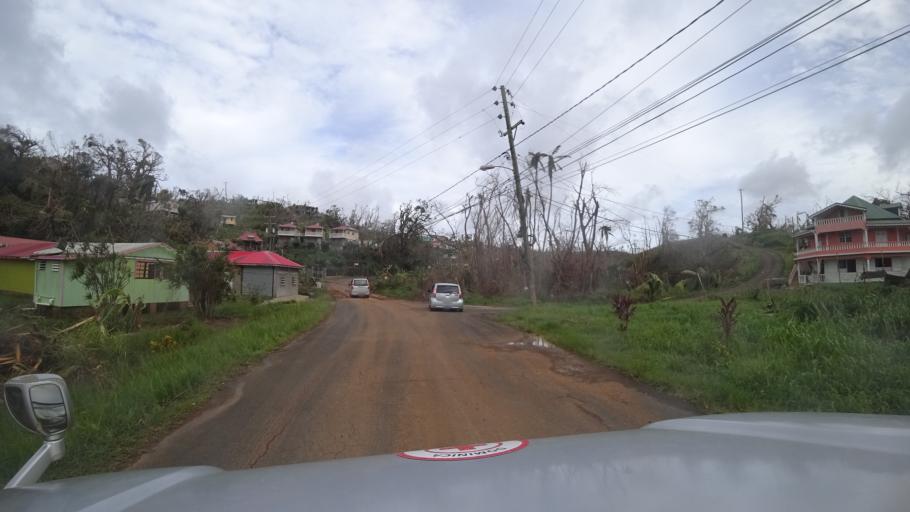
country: DM
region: Saint Andrew
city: Calibishie
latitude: 15.5935
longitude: -61.3453
